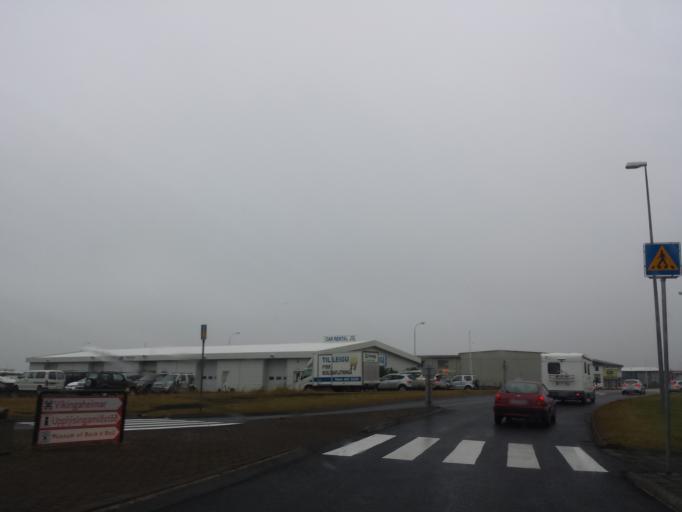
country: IS
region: Southern Peninsula
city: Reykjanesbaer
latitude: 63.9949
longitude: -22.5492
